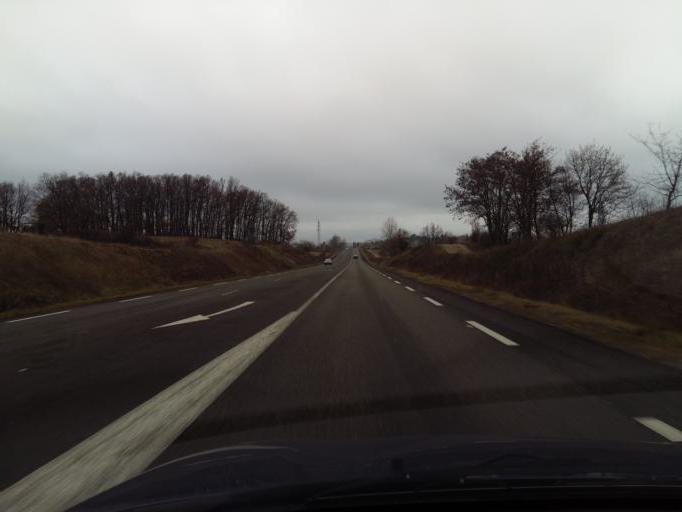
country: FR
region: Rhone-Alpes
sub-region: Departement de l'Ardeche
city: Saint-Cyr
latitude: 45.2559
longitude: 4.7315
